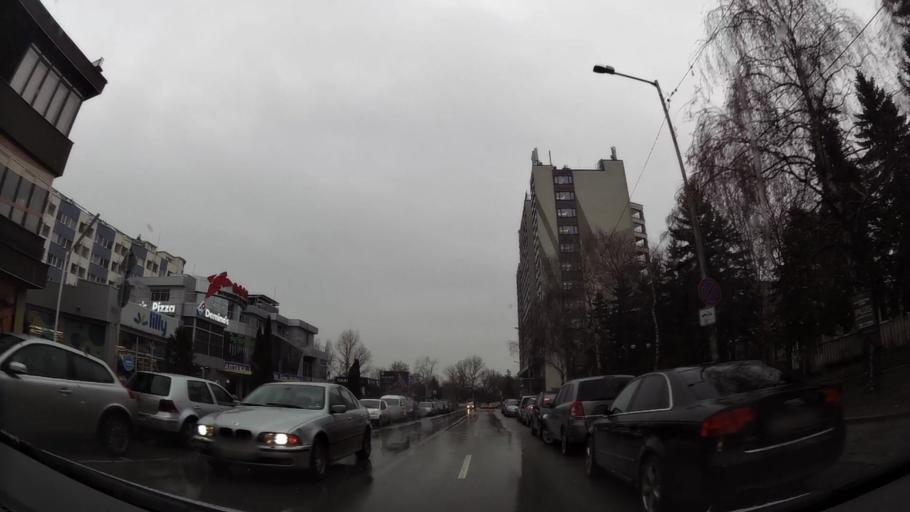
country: BG
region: Sofia-Capital
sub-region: Stolichna Obshtina
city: Sofia
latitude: 42.6536
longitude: 23.3456
